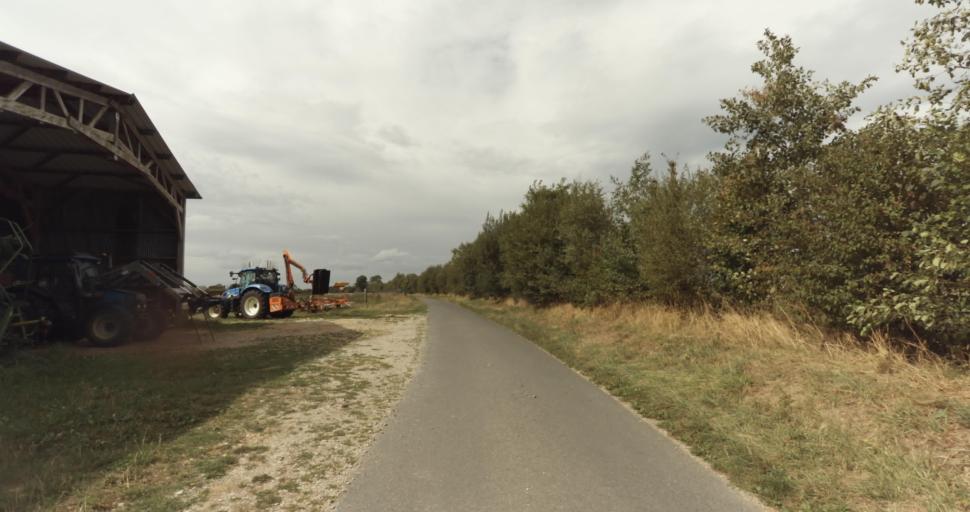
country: FR
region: Lower Normandy
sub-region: Departement du Calvados
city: Orbec
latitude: 48.9600
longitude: 0.3767
